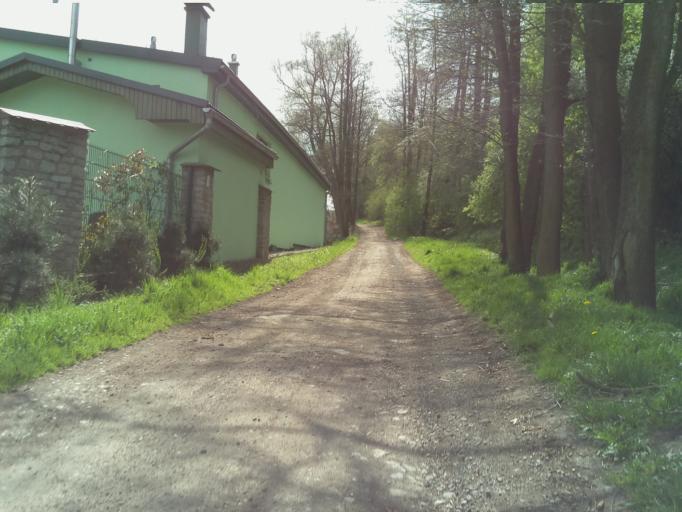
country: PL
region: Lower Silesian Voivodeship
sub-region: Powiat swidnicki
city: Swiebodzice
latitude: 50.8273
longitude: 16.3238
